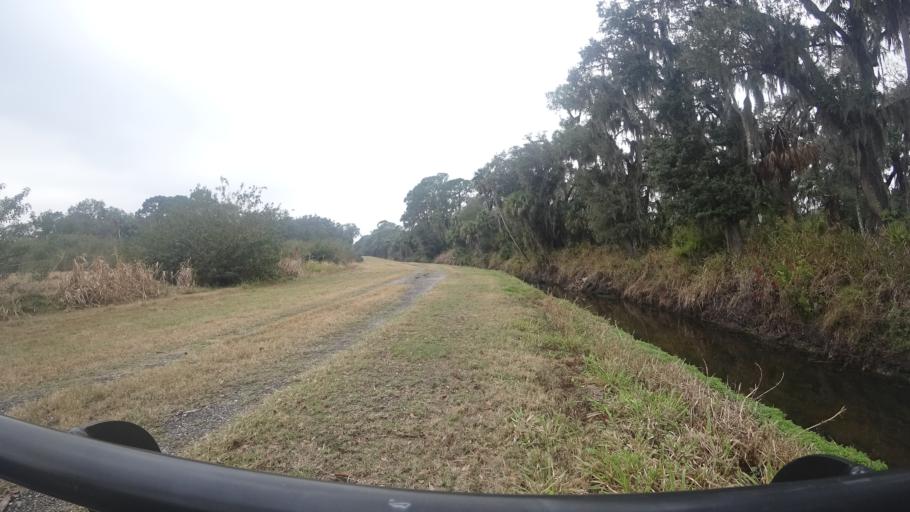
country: US
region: Florida
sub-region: Manatee County
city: Ellenton
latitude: 27.5913
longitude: -82.4889
